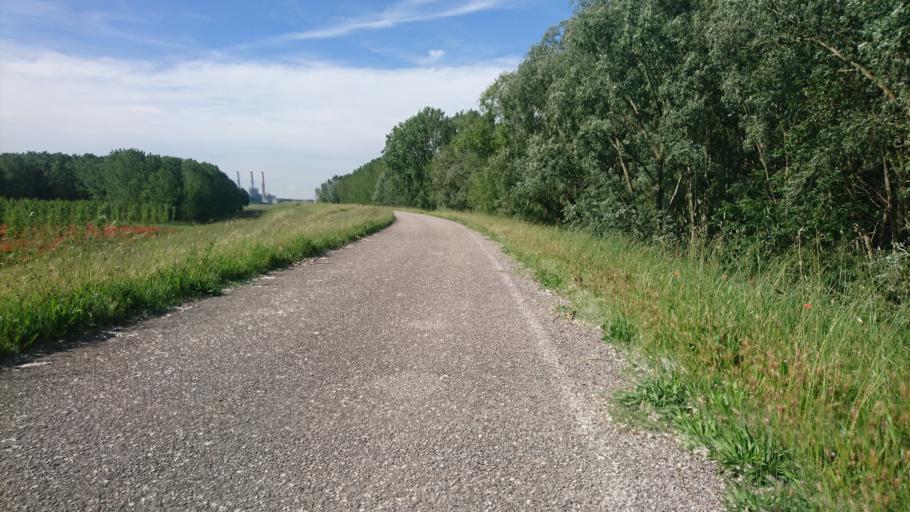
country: IT
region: Veneto
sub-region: Provincia di Rovigo
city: Bergantino
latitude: 45.0494
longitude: 11.2549
